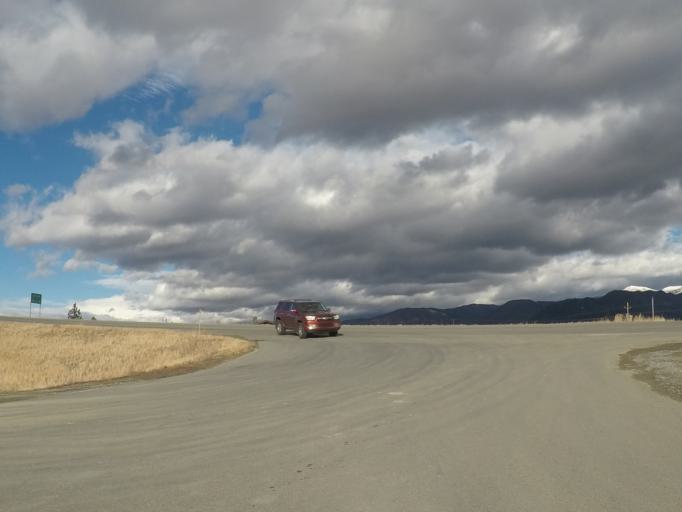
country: US
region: Montana
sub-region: Jefferson County
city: Boulder
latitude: 46.2445
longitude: -112.1170
